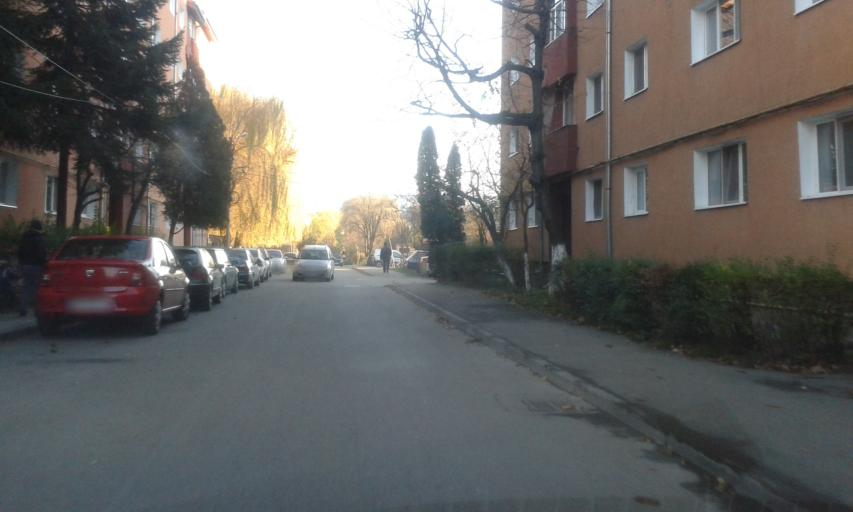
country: RO
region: Hunedoara
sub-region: Municipiul Petrosani
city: Petrosani
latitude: 45.4150
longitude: 23.3723
